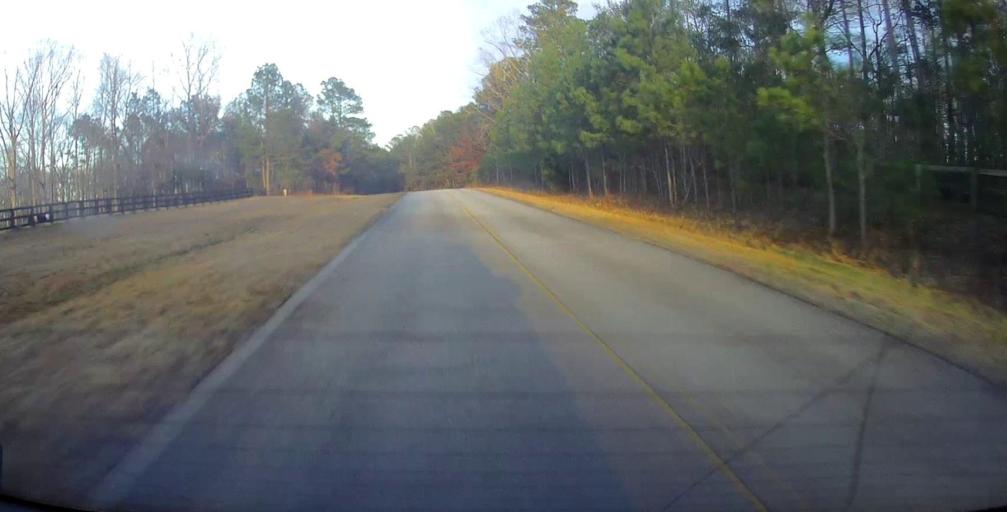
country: US
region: Georgia
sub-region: Harris County
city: Hamilton
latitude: 32.6049
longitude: -84.8741
